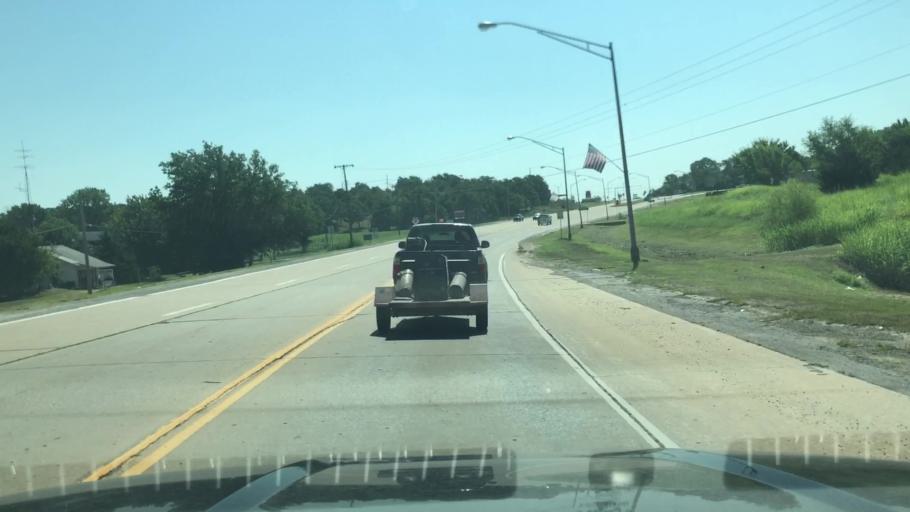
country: US
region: Oklahoma
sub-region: Creek County
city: Drumright
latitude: 35.9884
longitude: -96.5883
